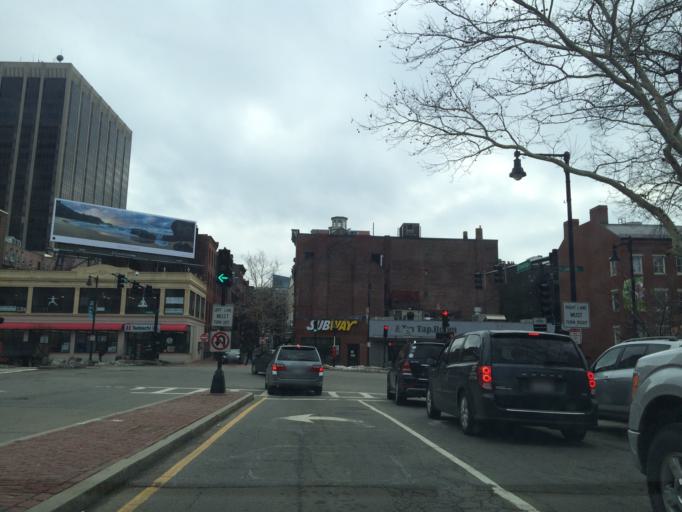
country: US
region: Massachusetts
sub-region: Suffolk County
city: Boston
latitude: 42.3616
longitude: -71.0638
